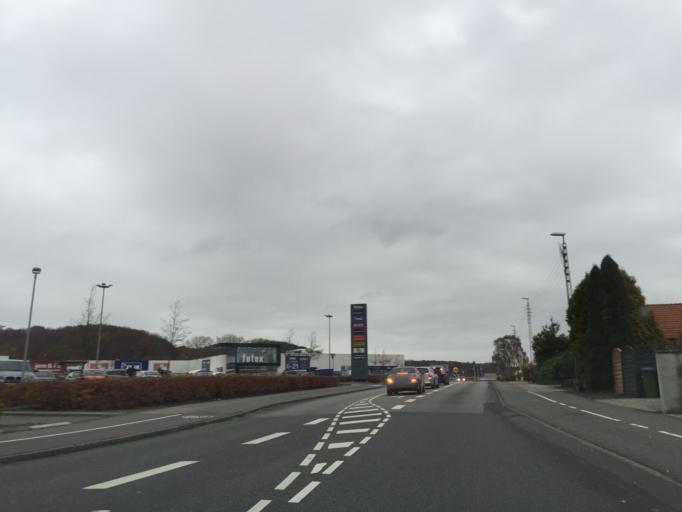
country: DK
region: Central Jutland
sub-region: Silkeborg Kommune
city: Silkeborg
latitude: 56.1843
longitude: 9.5456
